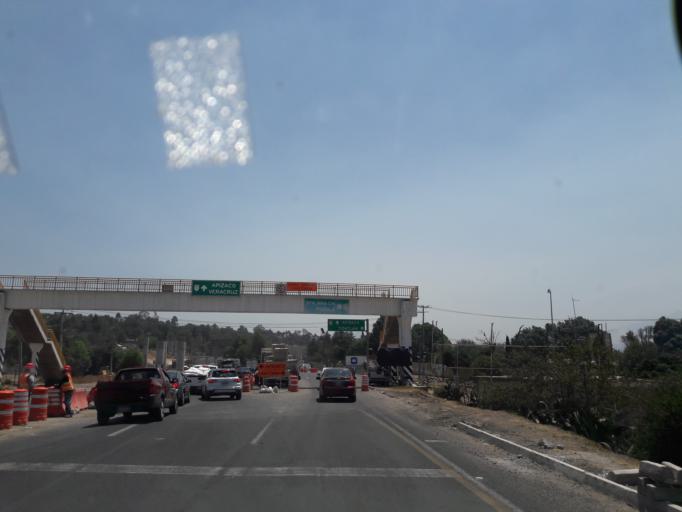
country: MX
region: Tlaxcala
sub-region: Apetatitlan de Antonio Carvajal
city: Tlatempan
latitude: 19.3426
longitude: -98.2015
